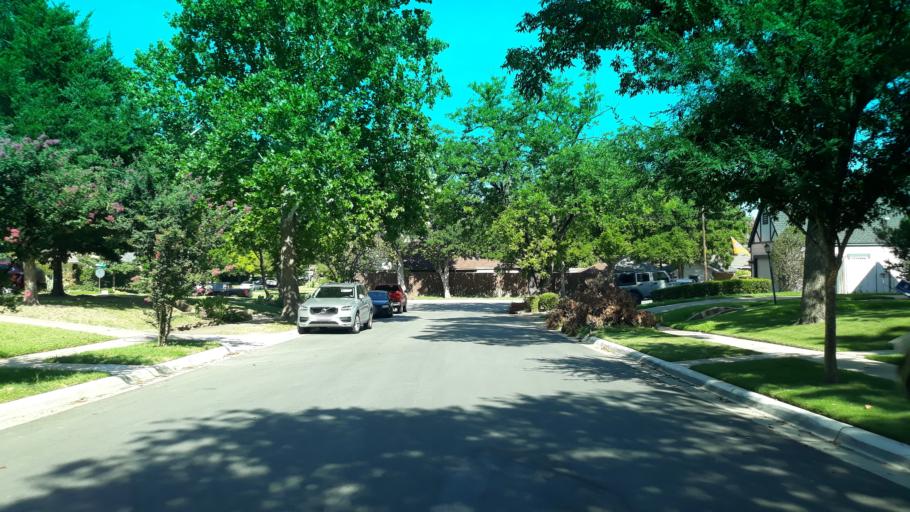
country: US
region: Texas
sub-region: Dallas County
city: Highland Park
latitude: 32.8198
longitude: -96.7622
